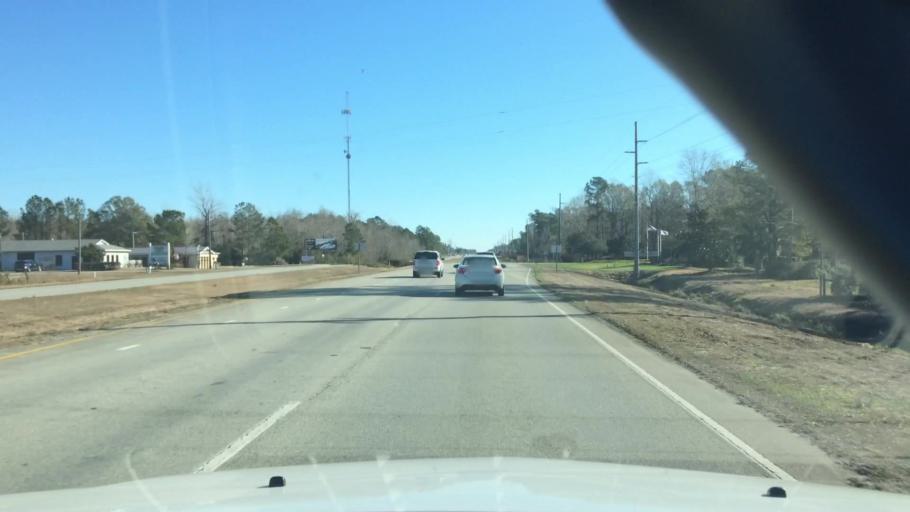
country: US
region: North Carolina
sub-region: Brunswick County
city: Sunset Beach
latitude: 33.9474
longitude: -78.4954
